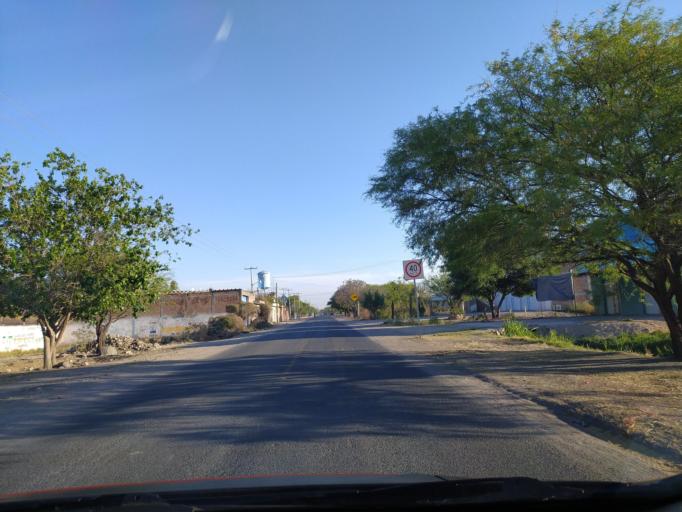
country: MX
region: Guanajuato
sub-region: San Francisco del Rincon
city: San Ignacio de Hidalgo
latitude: 20.9092
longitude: -101.8577
